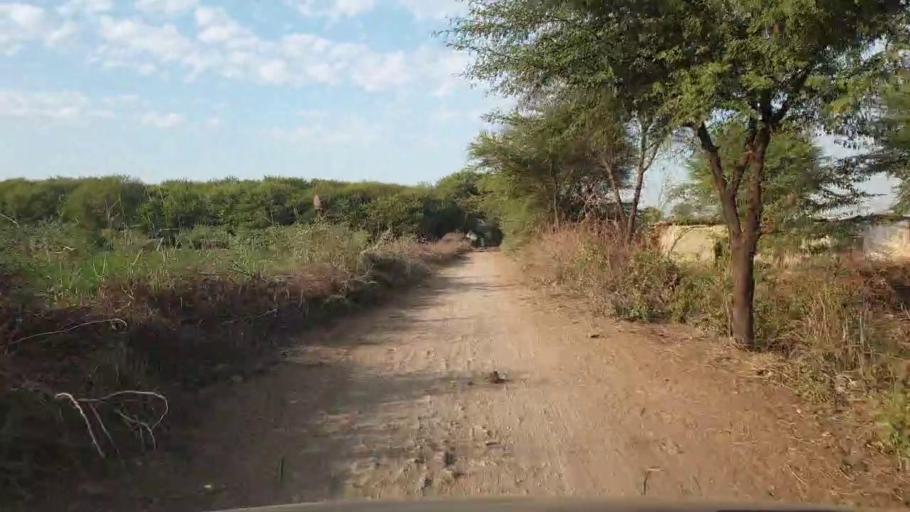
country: PK
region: Sindh
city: Sakrand
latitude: 26.0271
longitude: 68.3684
